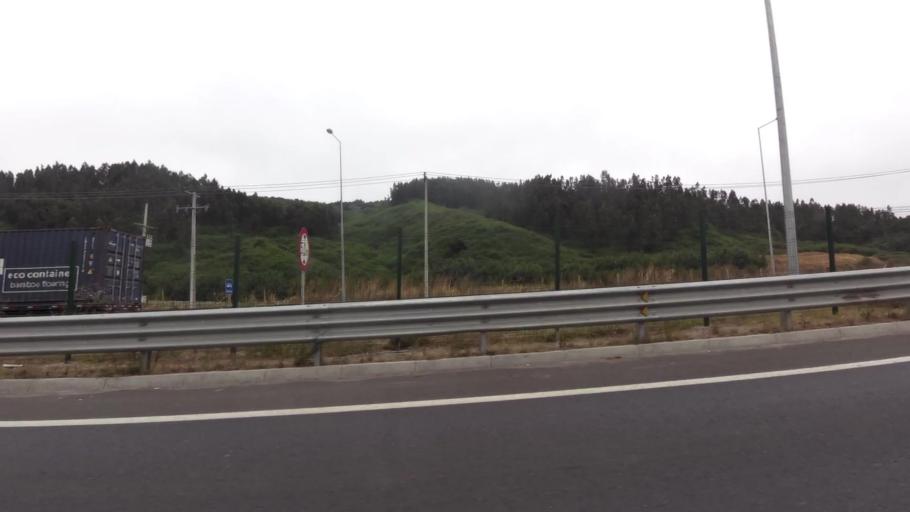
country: CL
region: Biobio
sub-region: Provincia de Concepcion
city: Concepcion
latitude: -36.8148
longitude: -73.0210
